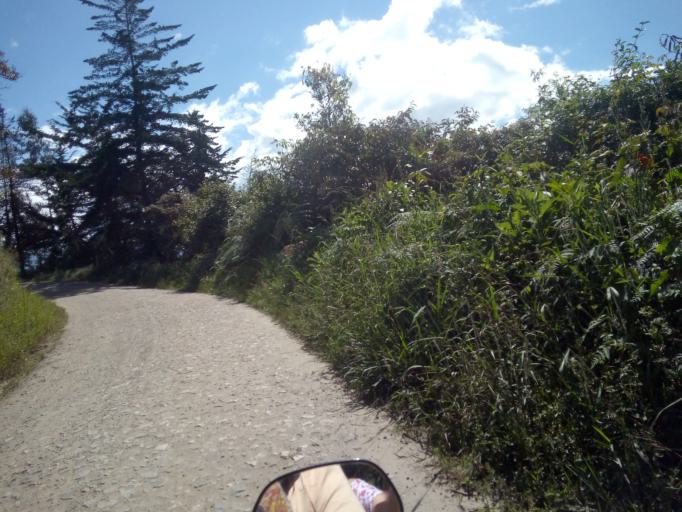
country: CO
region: Cundinamarca
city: Tenza
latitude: 5.1040
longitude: -73.4152
